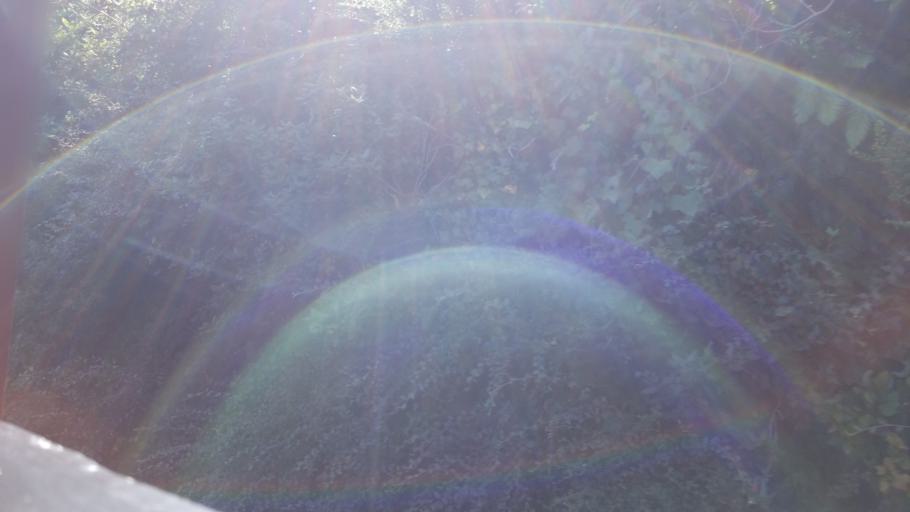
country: US
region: California
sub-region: Mendocino County
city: Fort Bragg
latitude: 39.4502
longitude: -123.7991
